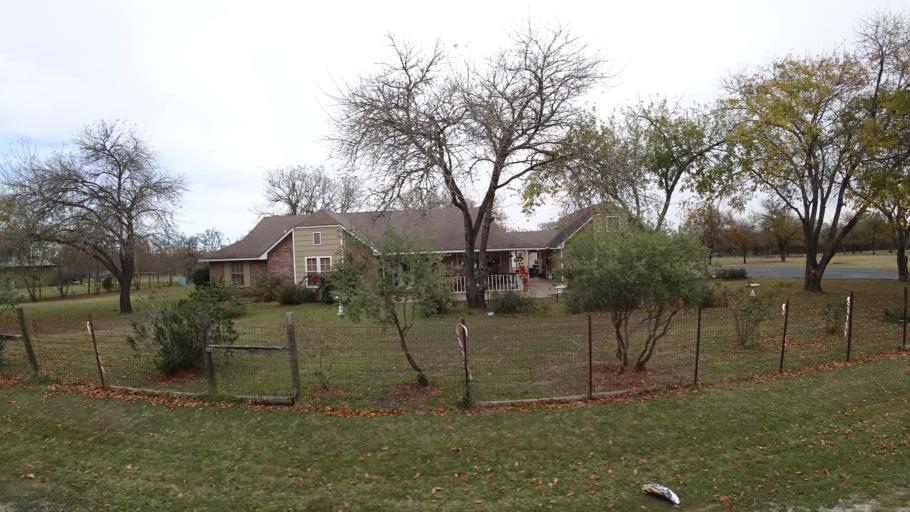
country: US
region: Texas
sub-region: Travis County
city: Garfield
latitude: 30.1066
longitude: -97.5740
